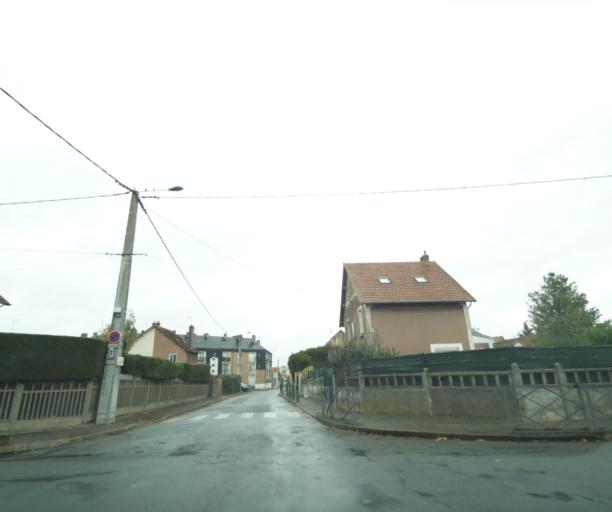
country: FR
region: Centre
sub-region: Departement d'Eure-et-Loir
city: Vernouillet
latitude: 48.7257
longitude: 1.3787
